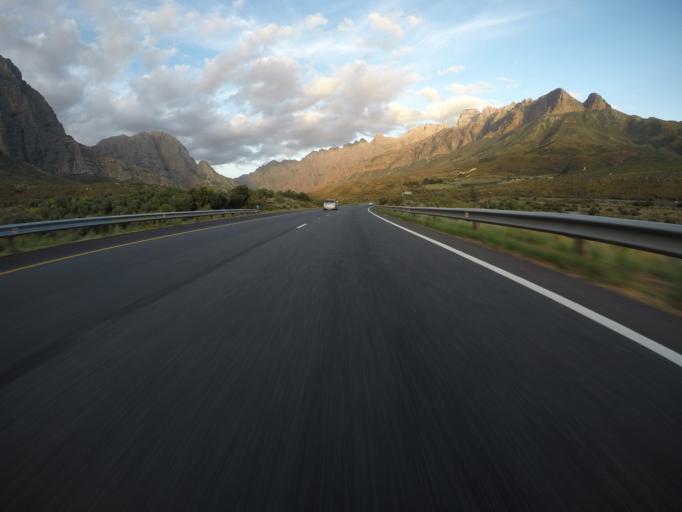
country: ZA
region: Western Cape
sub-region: Cape Winelands District Municipality
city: Paarl
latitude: -33.7261
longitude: 19.1332
